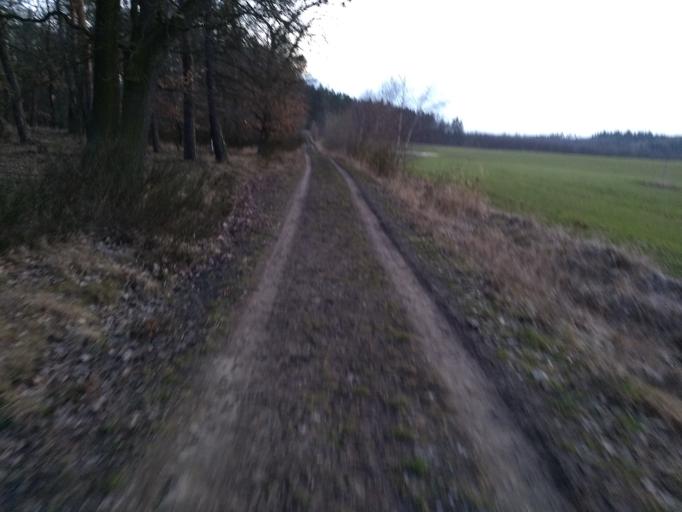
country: CZ
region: Central Bohemia
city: Unhost'
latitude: 50.0458
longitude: 14.1564
